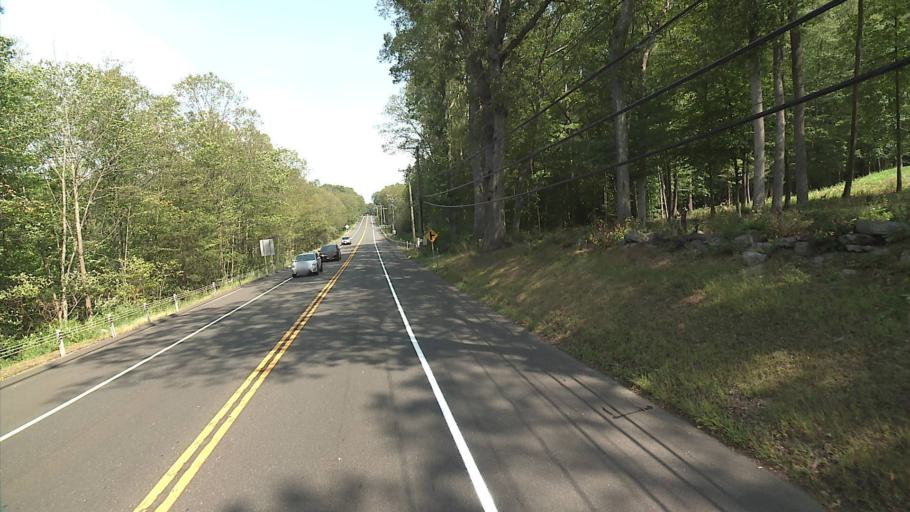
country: US
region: Connecticut
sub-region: New Haven County
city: Guilford
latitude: 41.3611
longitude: -72.6381
